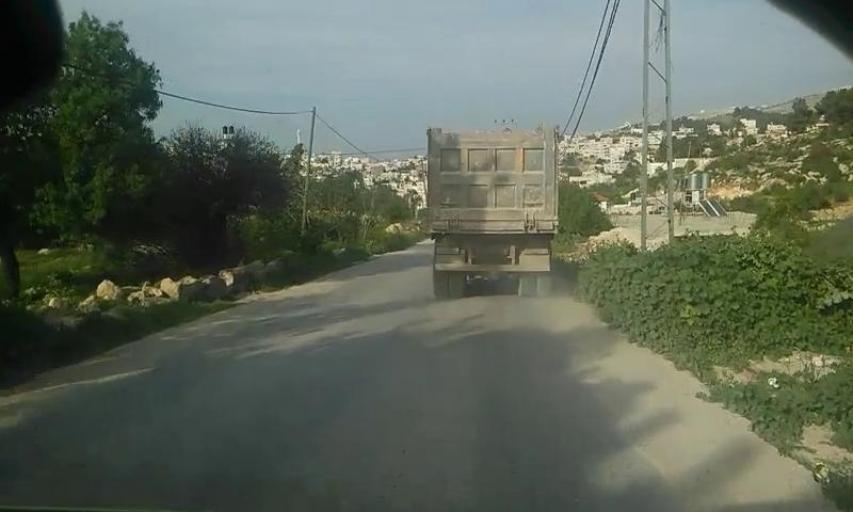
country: PS
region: West Bank
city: Bayt Ula
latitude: 31.5887
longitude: 35.0255
